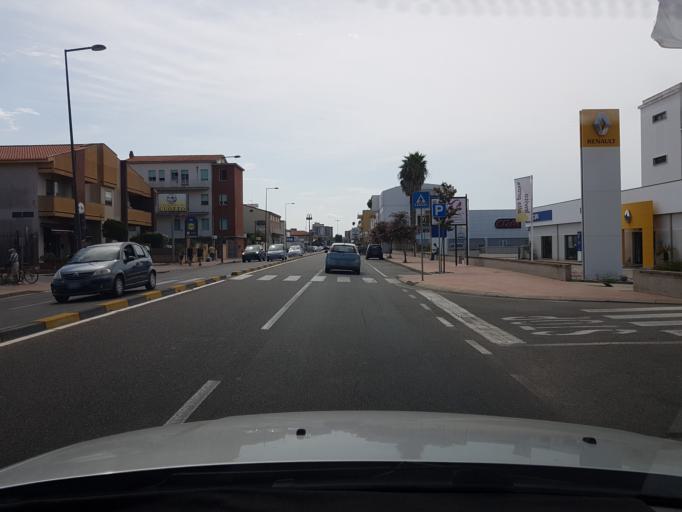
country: IT
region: Sardinia
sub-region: Provincia di Oristano
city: Oristano
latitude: 39.9139
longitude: 8.5861
